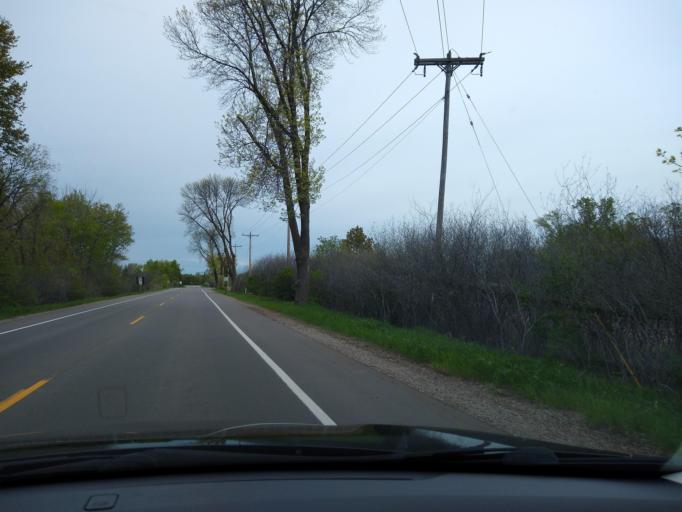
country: US
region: Michigan
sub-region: Delta County
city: Escanaba
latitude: 45.7720
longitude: -87.0695
